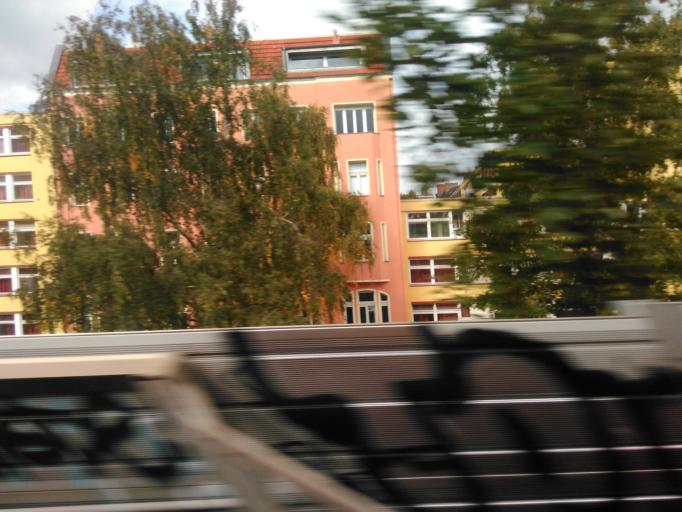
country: DE
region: Berlin
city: Wedding Bezirk
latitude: 52.5417
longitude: 13.3638
